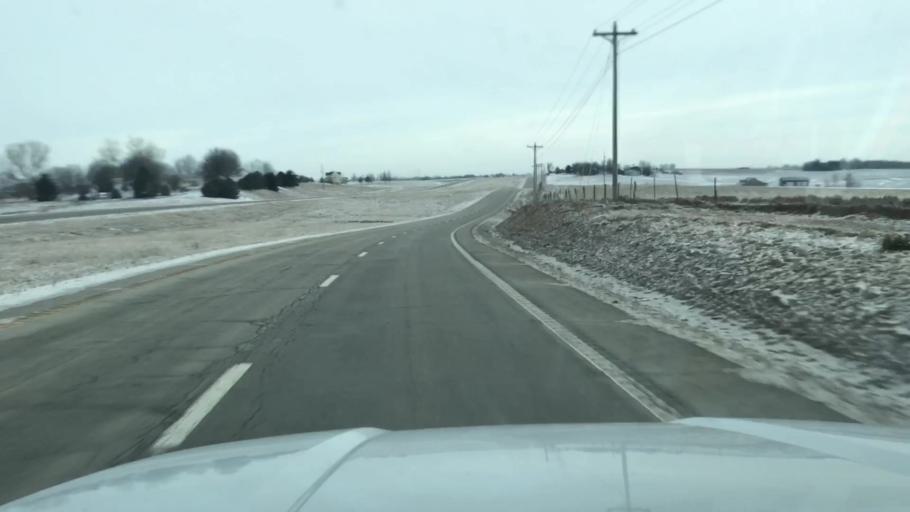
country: US
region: Missouri
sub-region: Andrew County
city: Savannah
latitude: 39.9845
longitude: -94.8799
